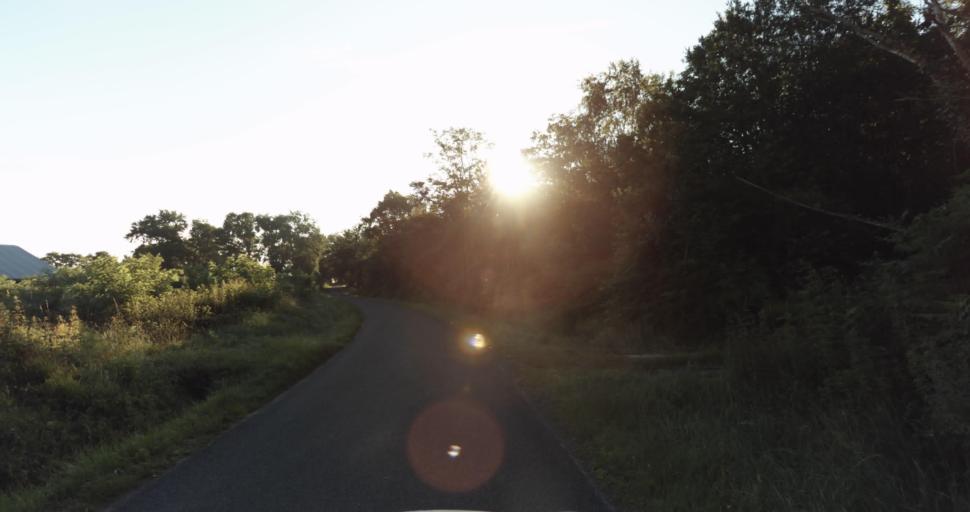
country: FR
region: Aquitaine
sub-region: Departement de la Gironde
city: Bazas
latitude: 44.4176
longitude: -0.2376
